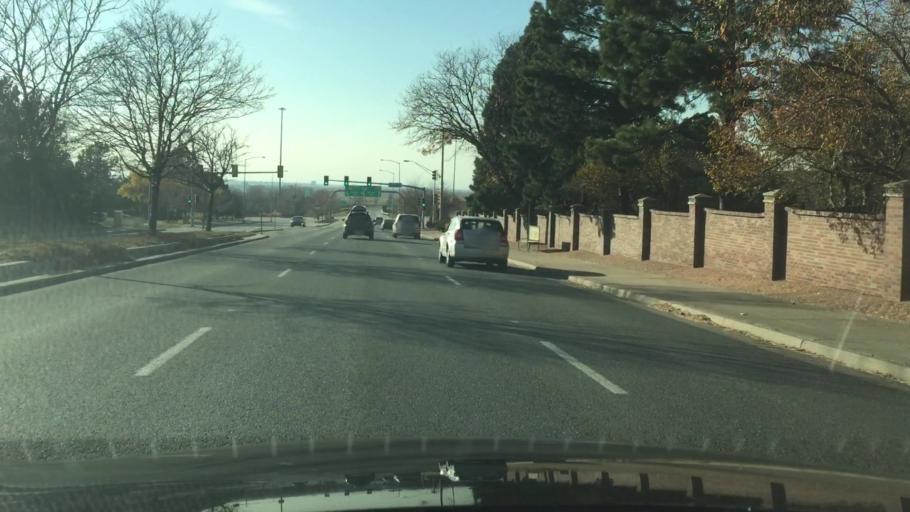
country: US
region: Colorado
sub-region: Arapahoe County
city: Dove Valley
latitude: 39.6531
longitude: -104.8268
